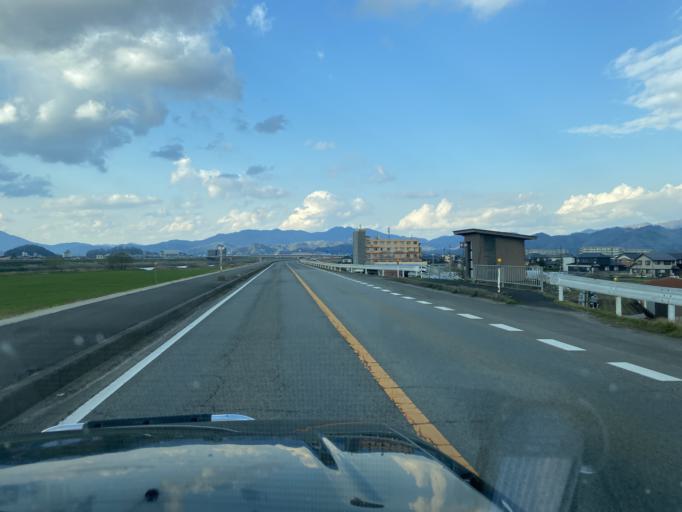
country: JP
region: Hyogo
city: Toyooka
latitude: 35.5184
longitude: 134.8244
